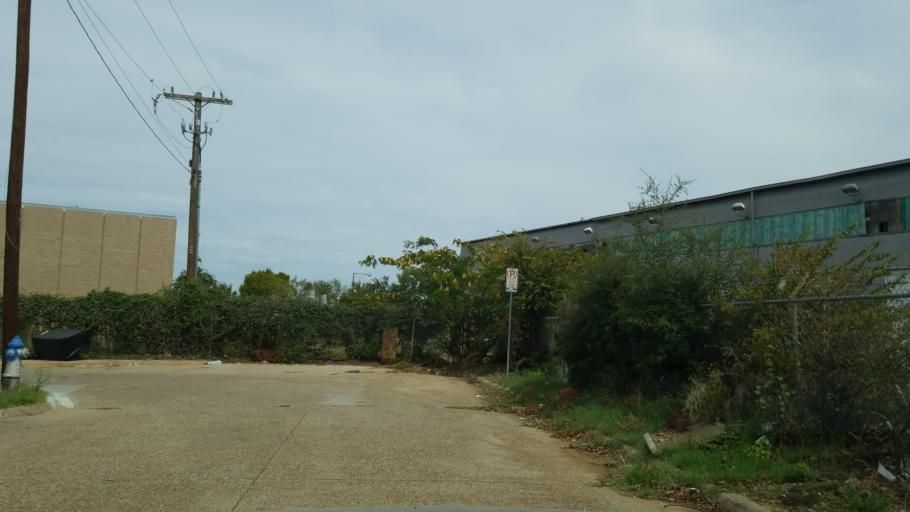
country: US
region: Texas
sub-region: Dallas County
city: Dallas
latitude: 32.7681
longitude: -96.7385
